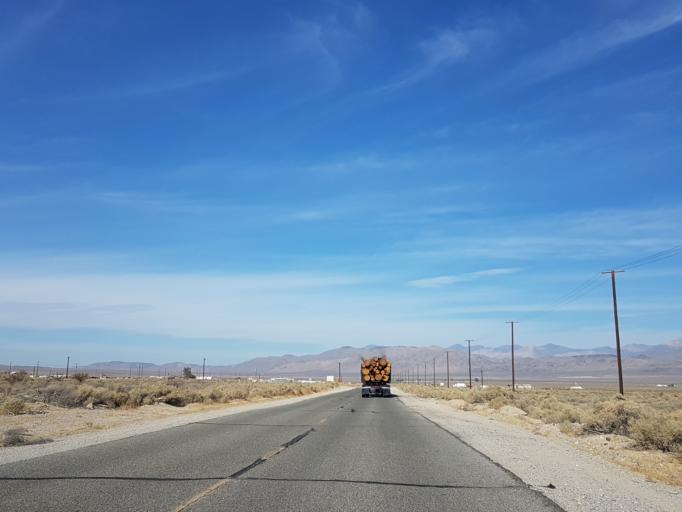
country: US
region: California
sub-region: San Bernardino County
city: Searles Valley
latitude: 35.7957
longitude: -117.3550
